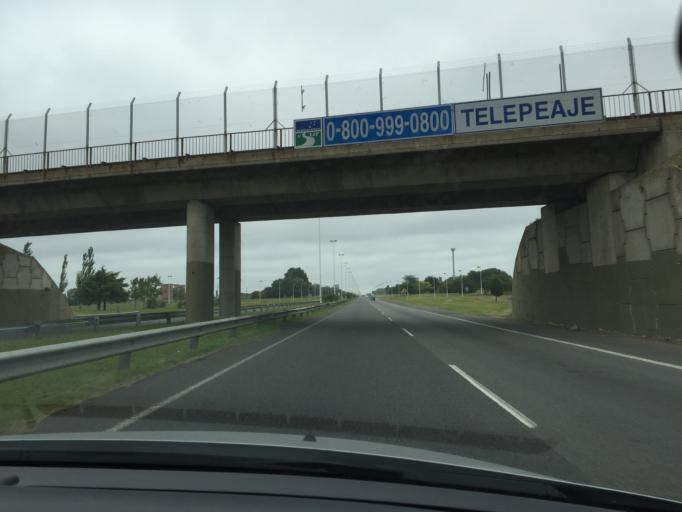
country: AR
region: Buenos Aires
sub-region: Partido de Ezeiza
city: Ezeiza
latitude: -34.8755
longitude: -58.5859
